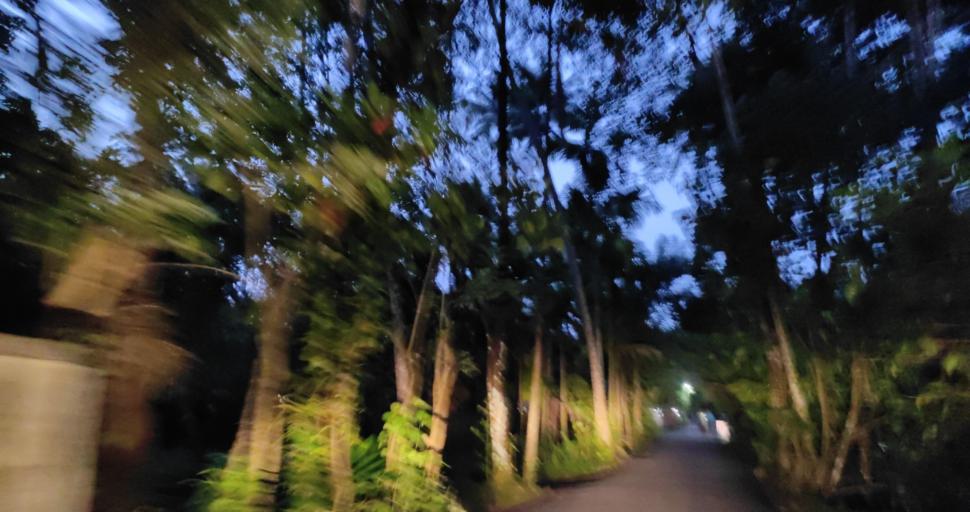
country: IN
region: Kerala
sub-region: Alappuzha
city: Vayalar
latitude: 9.7233
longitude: 76.2911
